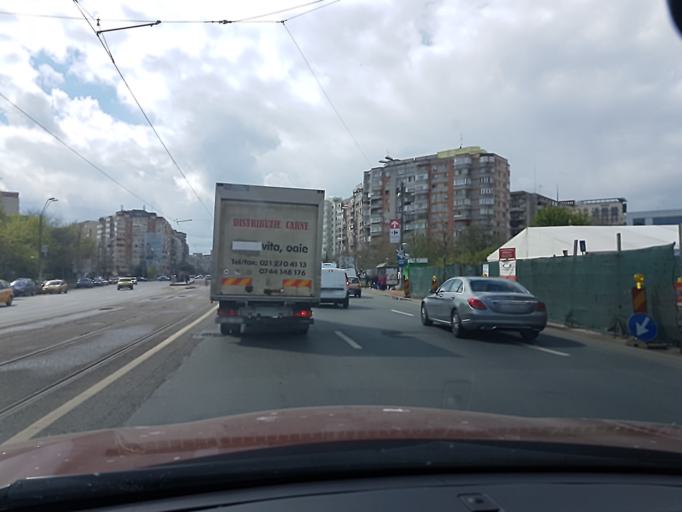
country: RO
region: Bucuresti
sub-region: Municipiul Bucuresti
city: Bucharest
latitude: 44.4260
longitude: 26.1376
